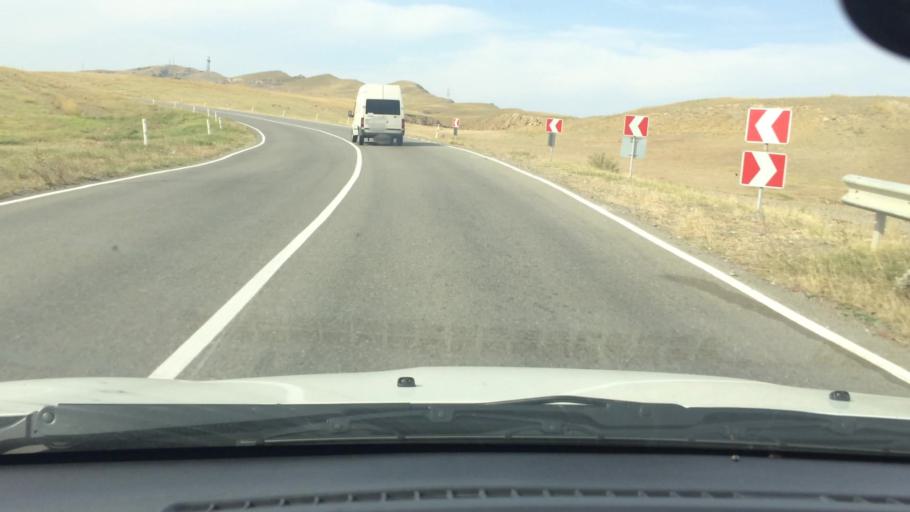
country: GE
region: Kvemo Kartli
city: Rust'avi
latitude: 41.5324
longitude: 44.9769
